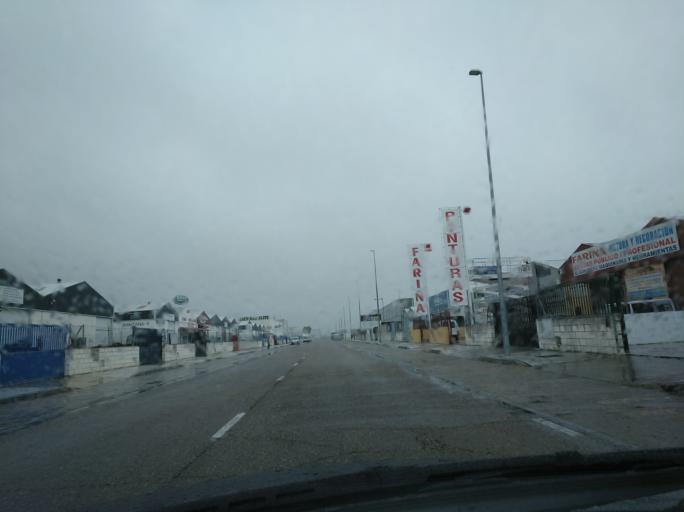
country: ES
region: Extremadura
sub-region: Provincia de Badajoz
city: Badajoz
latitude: 38.9007
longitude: -6.9948
